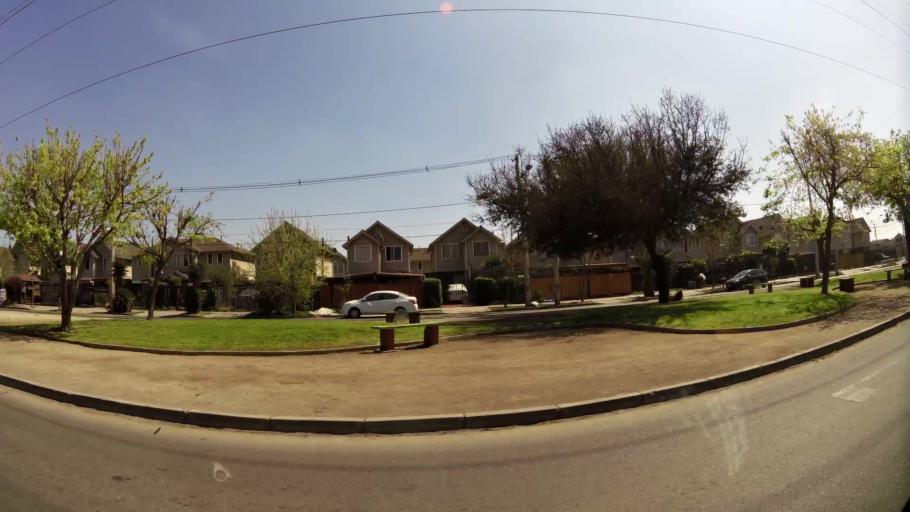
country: CL
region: Santiago Metropolitan
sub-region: Provincia de Santiago
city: Lo Prado
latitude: -33.3635
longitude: -70.7186
